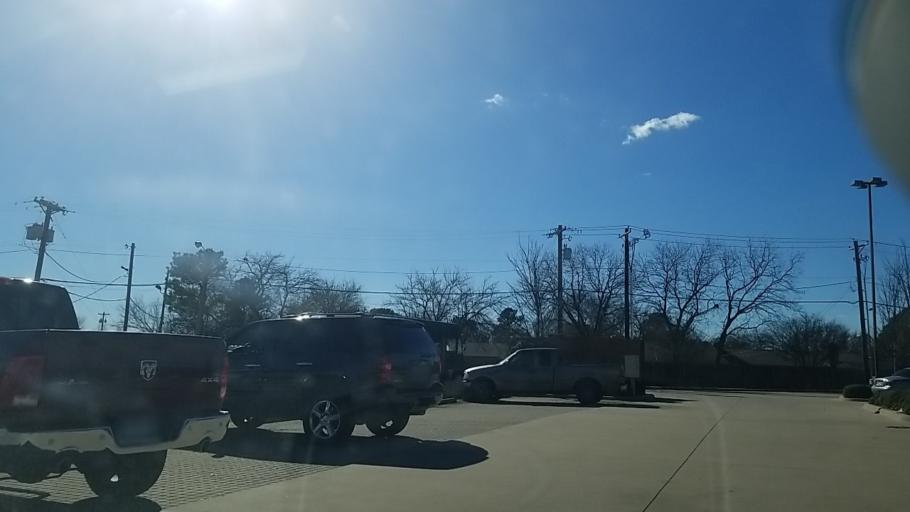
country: US
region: Texas
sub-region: Denton County
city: Corinth
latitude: 33.1734
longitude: -97.0912
